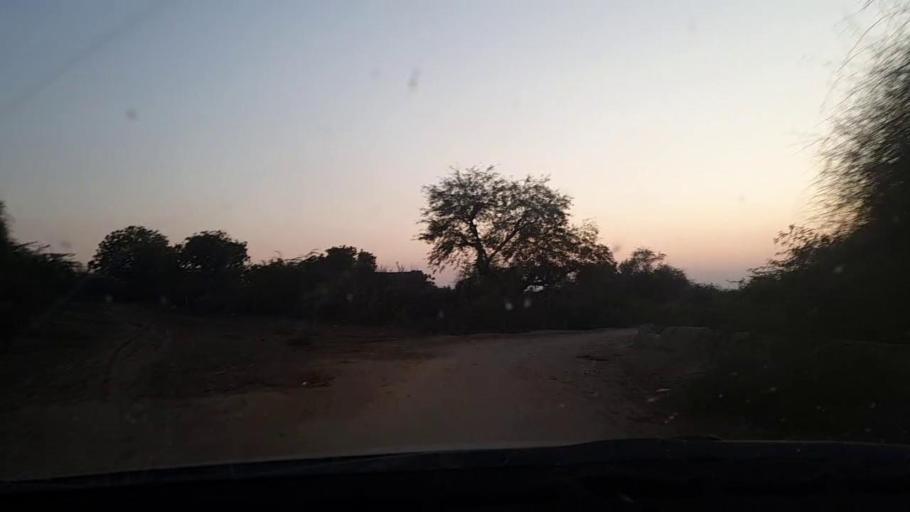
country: PK
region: Sindh
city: Tando Mittha Khan
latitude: 25.9221
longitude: 69.3283
